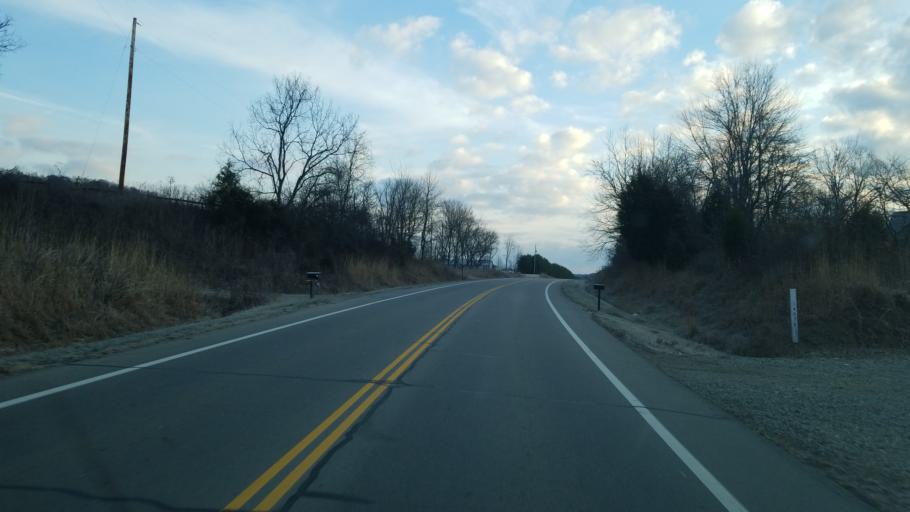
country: US
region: Ohio
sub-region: Ross County
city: North Fork Village
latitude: 39.3094
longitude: -83.1268
